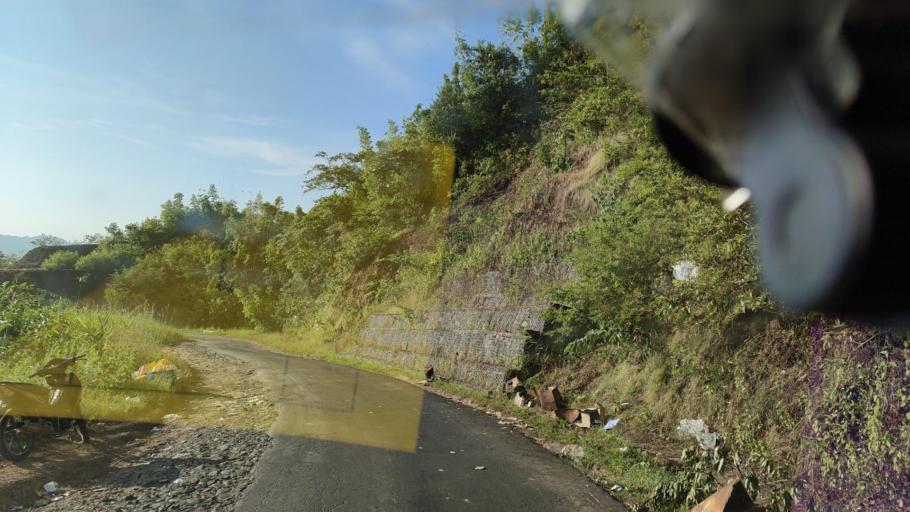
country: MM
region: Magway
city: Minbu
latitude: 19.8755
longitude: 94.1650
